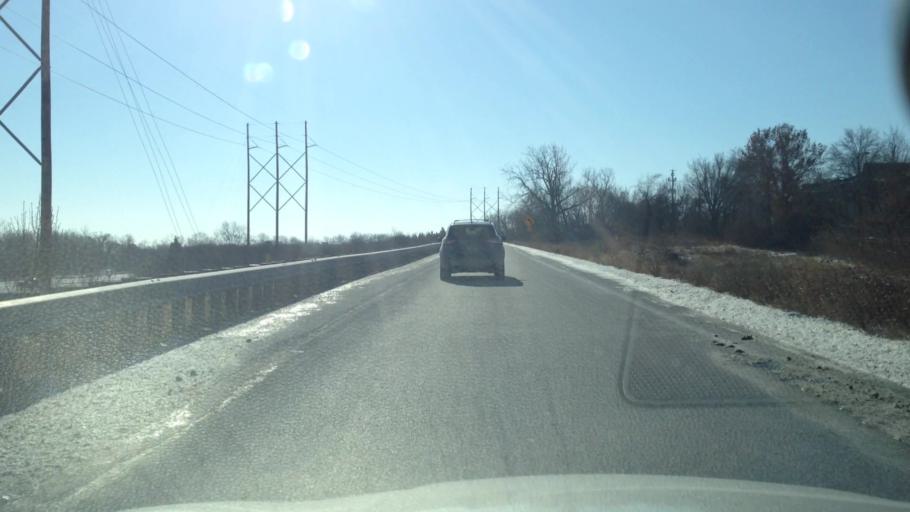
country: US
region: Missouri
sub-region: Clay County
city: Gladstone
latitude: 39.1734
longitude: -94.5604
